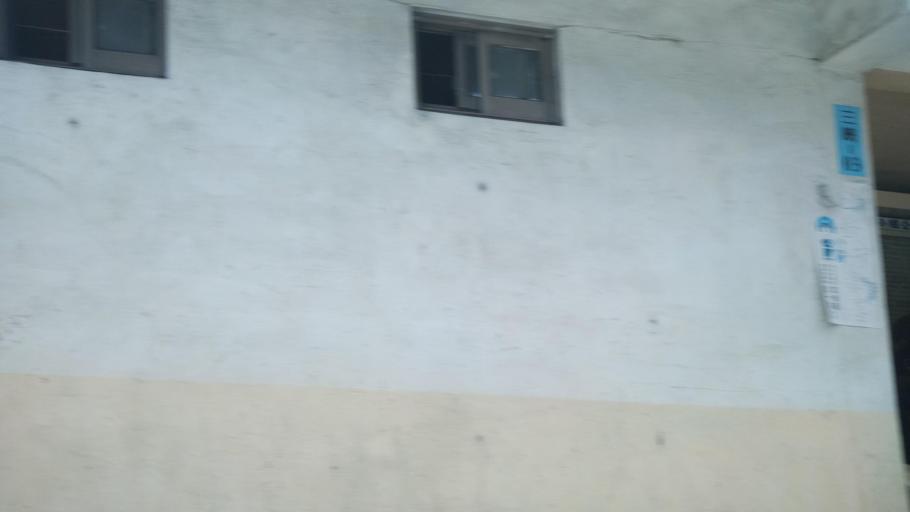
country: TW
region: Taipei
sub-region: Taipei
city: Banqiao
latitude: 24.9321
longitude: 121.4547
